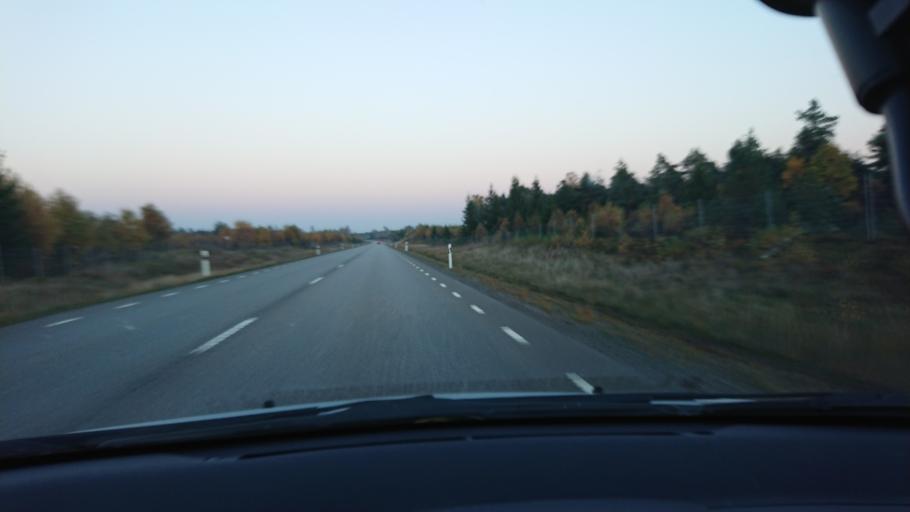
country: SE
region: Kronoberg
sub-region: Markaryds Kommun
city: Stromsnasbruk
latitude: 56.7525
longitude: 13.5434
